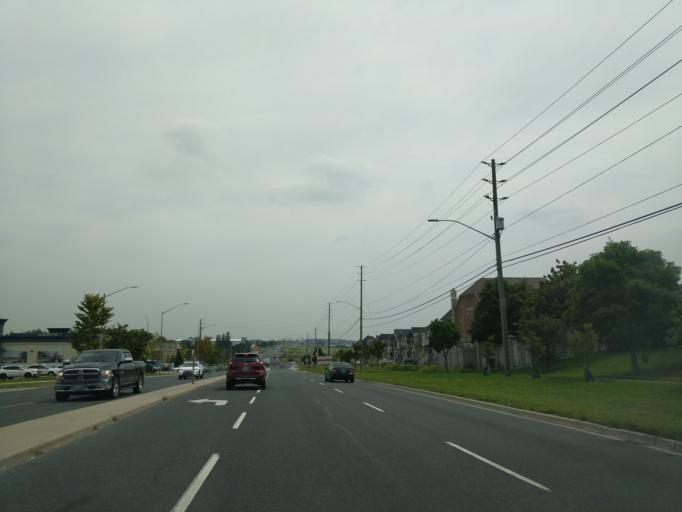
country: CA
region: Ontario
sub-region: York
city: Richmond Hill
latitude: 43.8793
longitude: -79.3954
